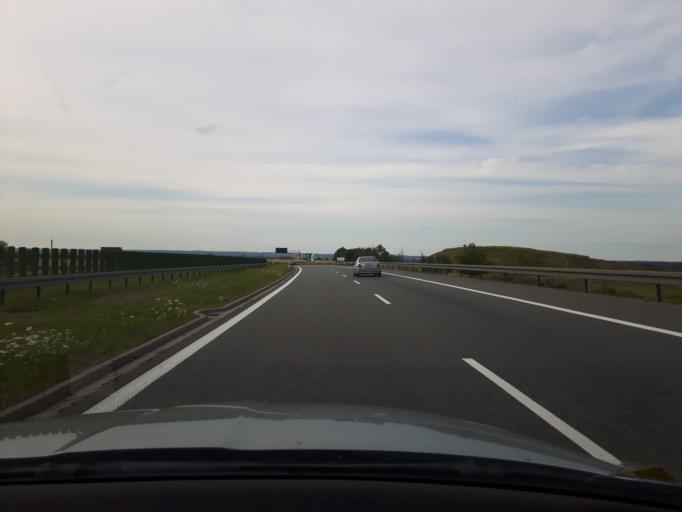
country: PL
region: Warmian-Masurian Voivodeship
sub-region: Powiat elblaski
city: Paslek
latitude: 54.0320
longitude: 19.6750
